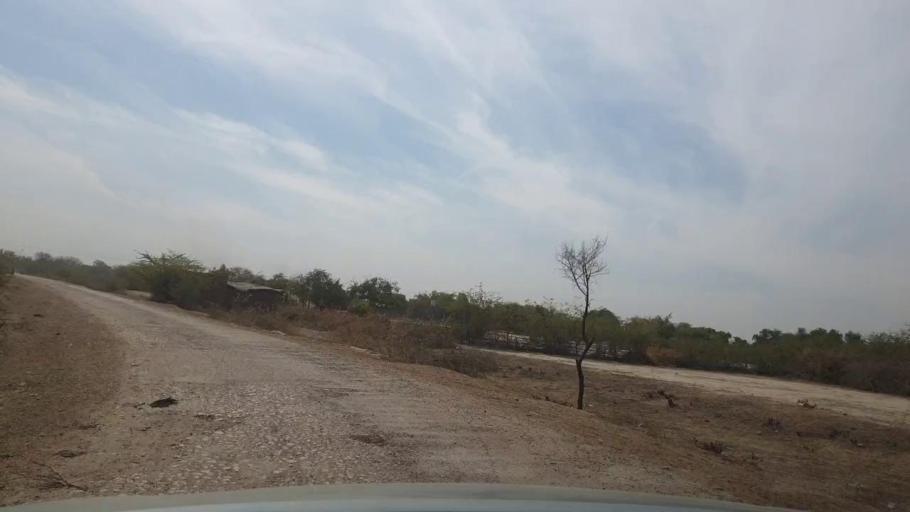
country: PK
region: Sindh
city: Nabisar
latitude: 25.0838
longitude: 69.5988
